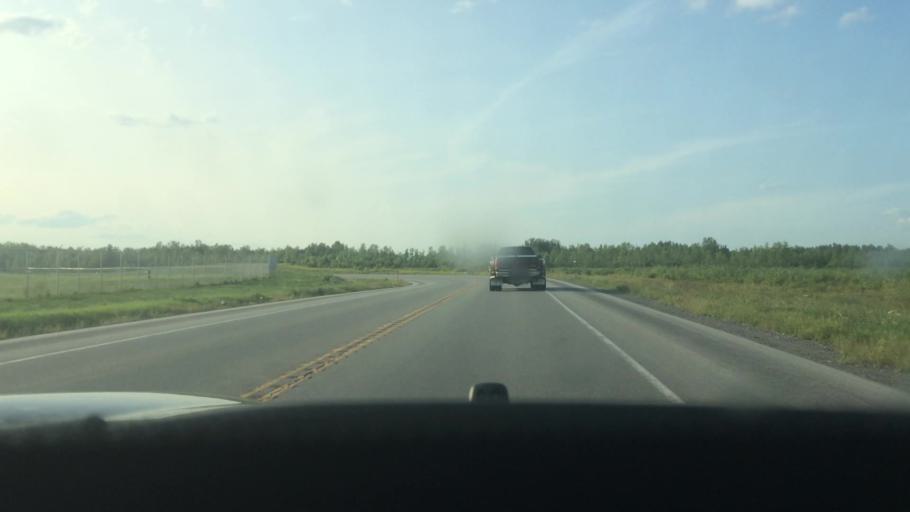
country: US
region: New York
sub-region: St. Lawrence County
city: Ogdensburg
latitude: 44.6834
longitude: -75.4460
